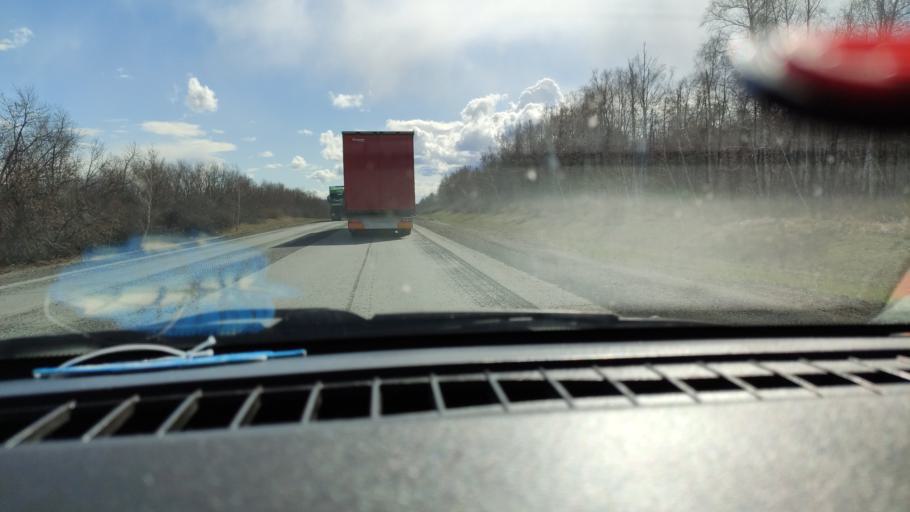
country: RU
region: Saratov
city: Dukhovnitskoye
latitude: 52.6339
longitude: 48.1863
